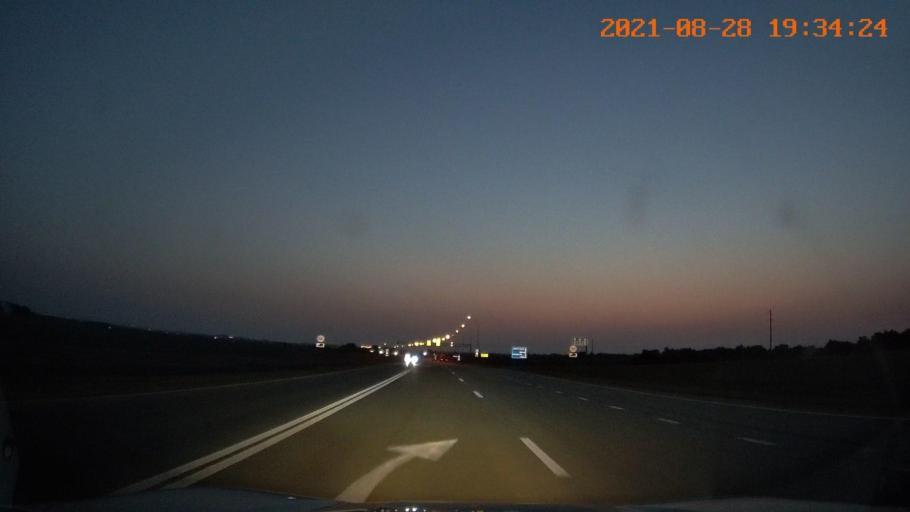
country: RU
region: Adygeya
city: Adygeysk
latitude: 44.9164
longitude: 39.2827
